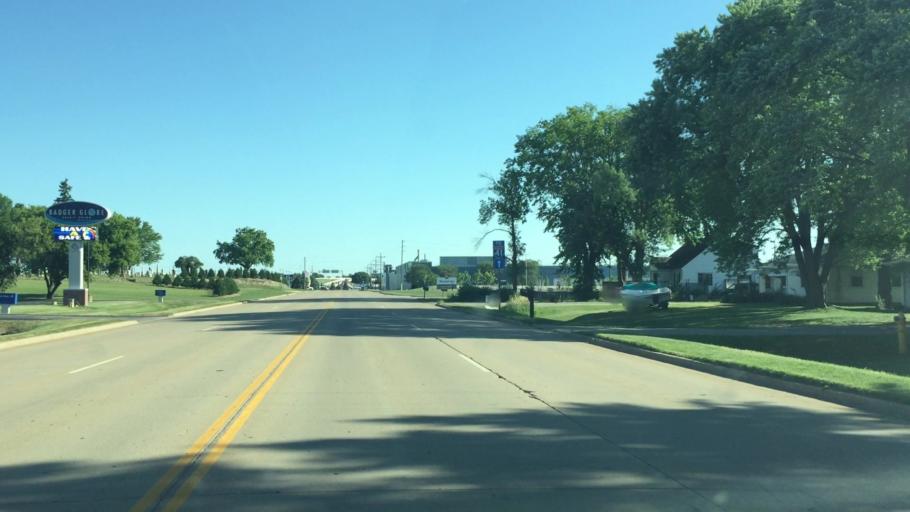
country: US
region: Wisconsin
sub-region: Winnebago County
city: Neenah
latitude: 44.1936
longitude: -88.4851
